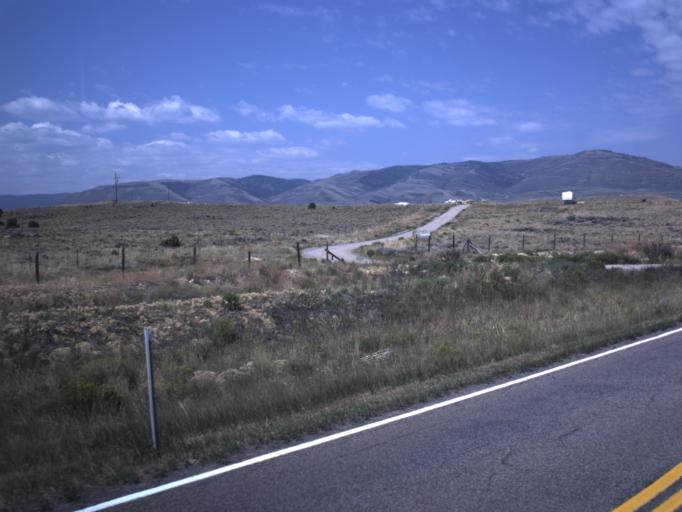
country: US
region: Utah
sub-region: Daggett County
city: Manila
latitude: 40.9789
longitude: -109.8049
